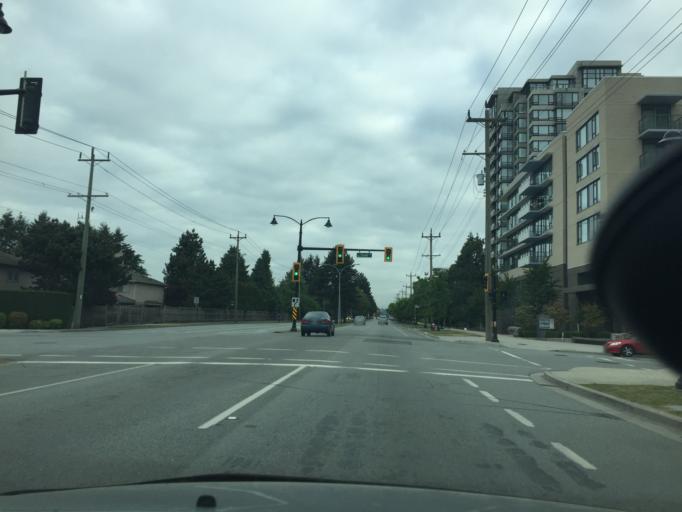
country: CA
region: British Columbia
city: Richmond
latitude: 49.1660
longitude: -123.1246
